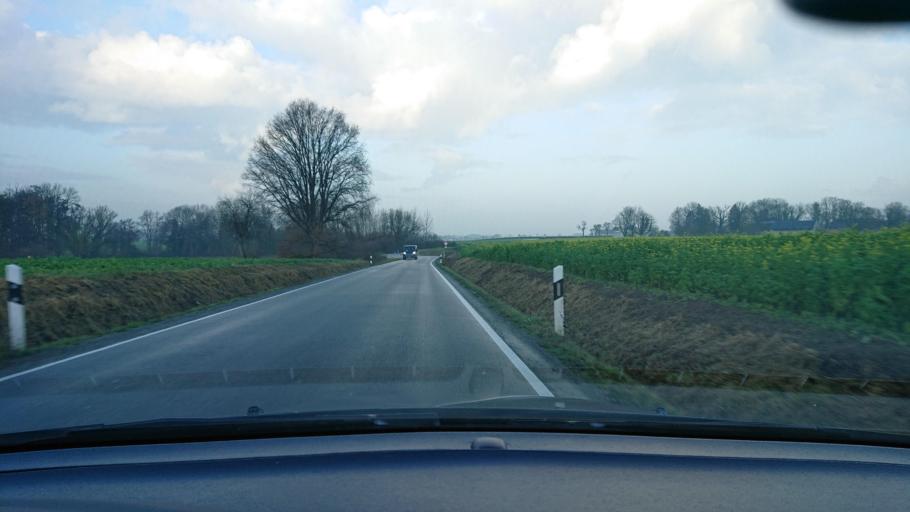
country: DE
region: North Rhine-Westphalia
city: Erwitte
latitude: 51.6272
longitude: 8.2779
